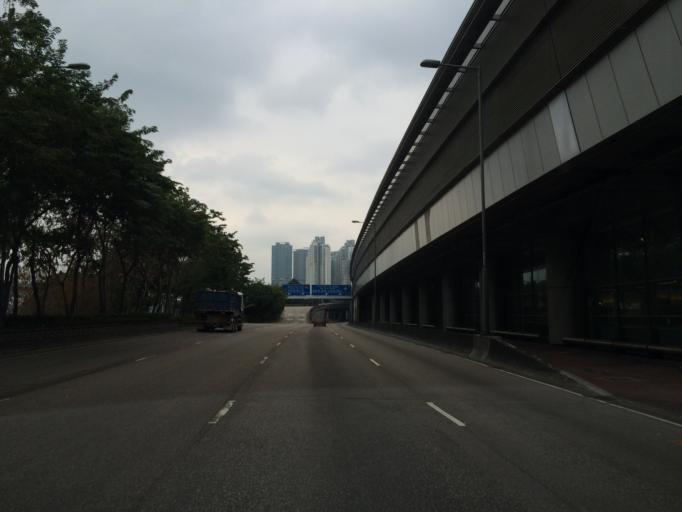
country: HK
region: Sham Shui Po
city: Sham Shui Po
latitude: 22.3256
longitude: 114.1539
